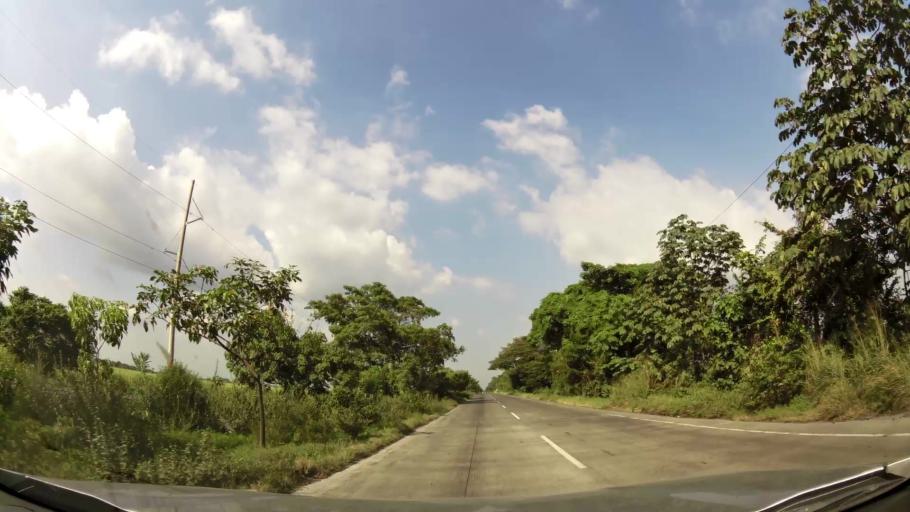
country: GT
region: Escuintla
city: Puerto San Jose
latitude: 14.0186
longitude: -90.7834
